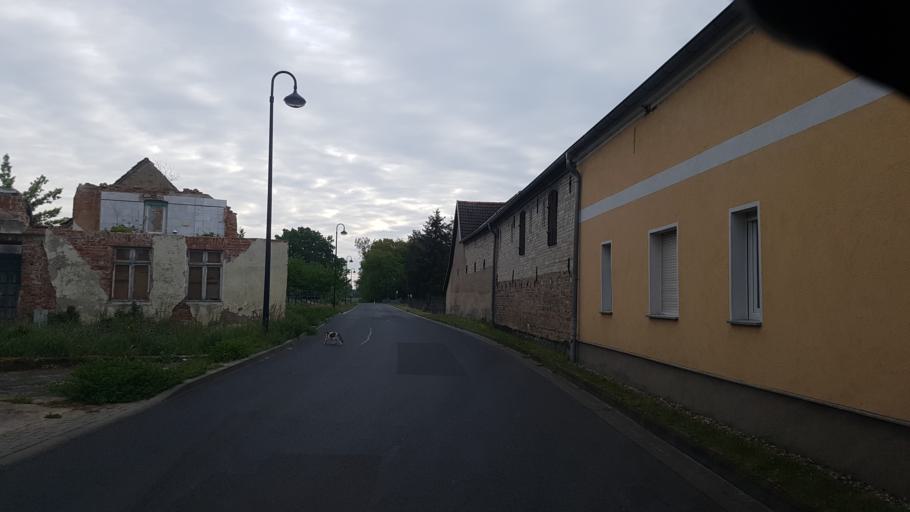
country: DE
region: Brandenburg
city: Beelitz
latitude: 52.1520
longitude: 13.0505
